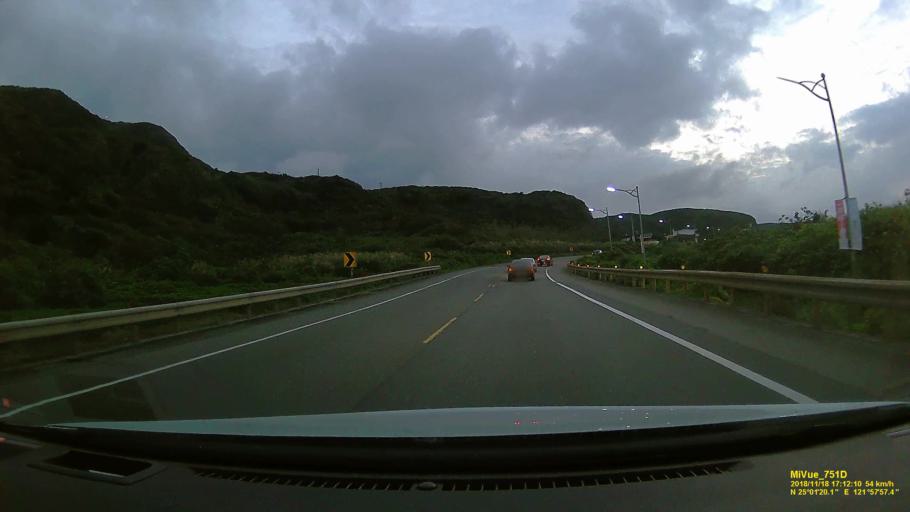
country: TW
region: Taiwan
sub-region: Keelung
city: Keelung
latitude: 25.0221
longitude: 121.9657
